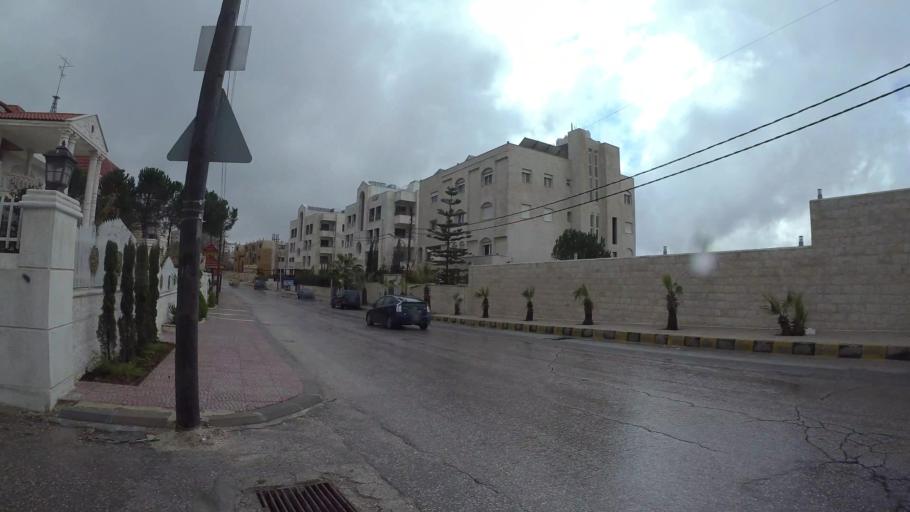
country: JO
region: Amman
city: Al Jubayhah
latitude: 32.0336
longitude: 35.8558
